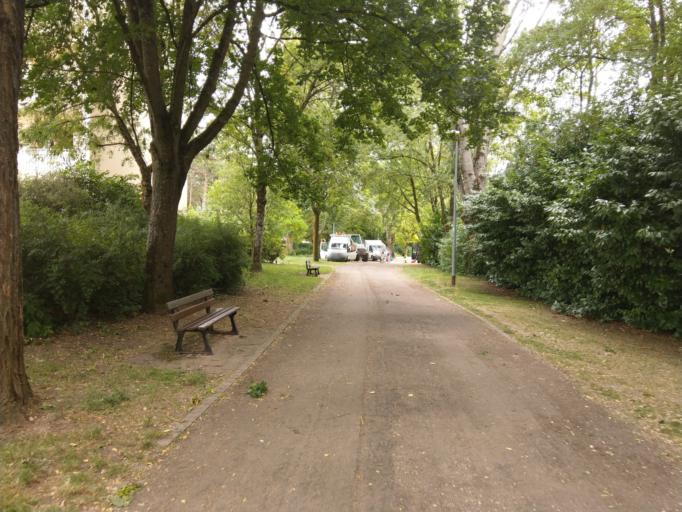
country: FR
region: Bourgogne
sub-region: Departement de la Cote-d'Or
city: Dijon
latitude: 47.3189
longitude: 5.0229
